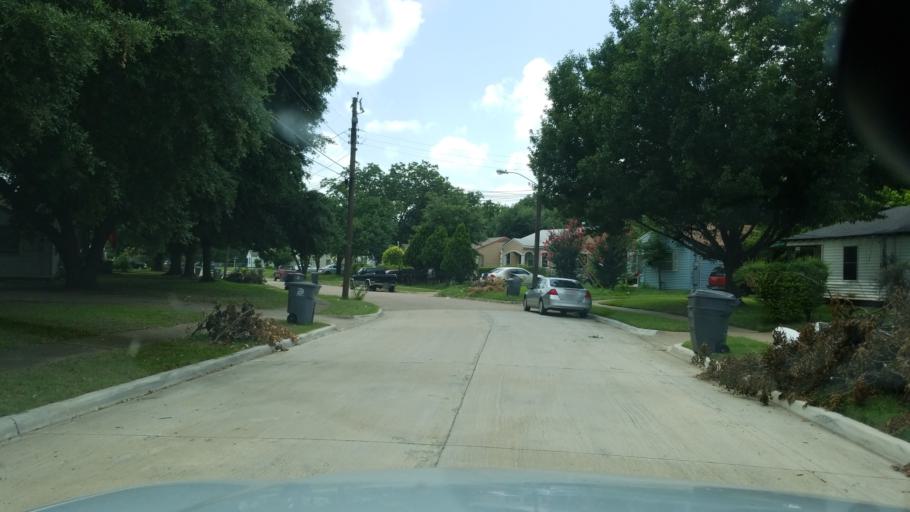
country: US
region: Texas
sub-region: Dallas County
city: Dallas
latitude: 32.8150
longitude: -96.8596
